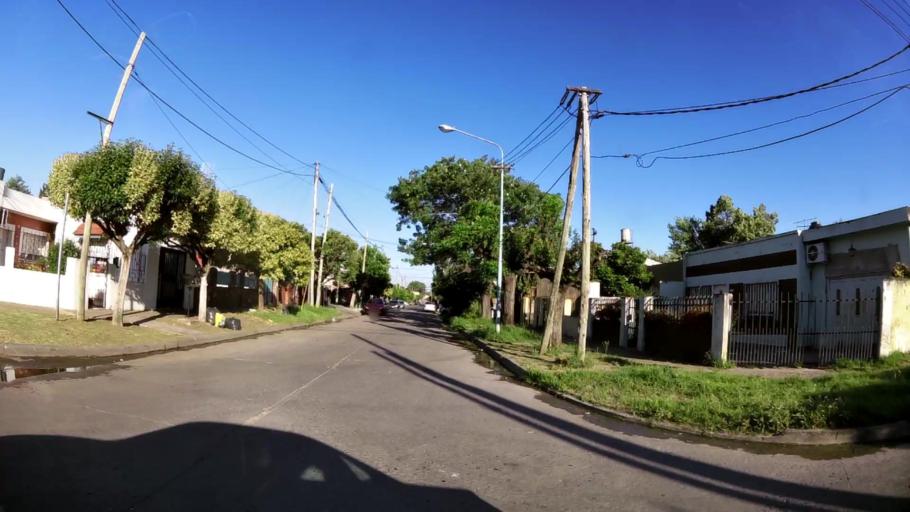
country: AR
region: Buenos Aires
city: Ituzaingo
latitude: -34.6874
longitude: -58.6420
